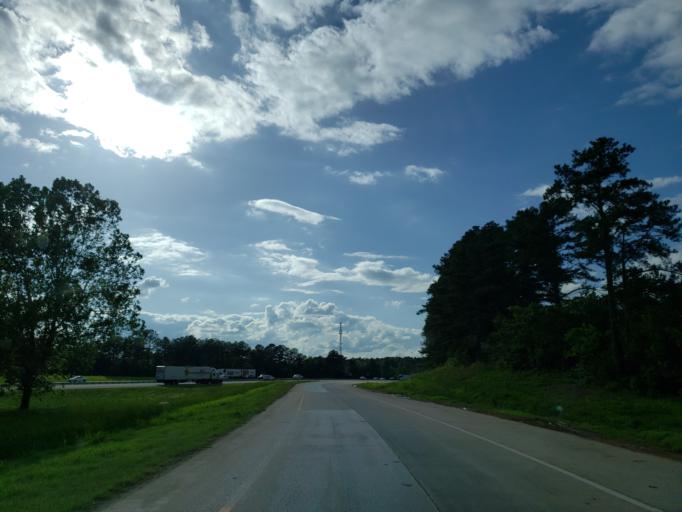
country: US
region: Georgia
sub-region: Bartow County
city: Cartersville
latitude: 34.2748
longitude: -84.8113
